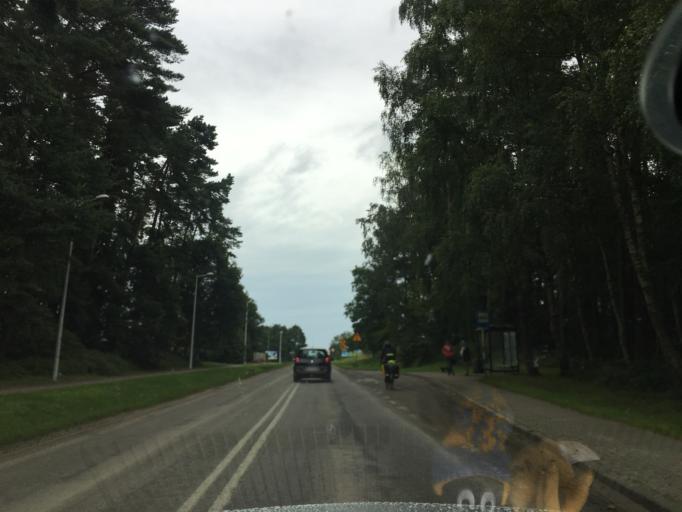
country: PL
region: West Pomeranian Voivodeship
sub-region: Powiat gryficki
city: Pobierowo
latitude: 54.0664
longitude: 14.9709
